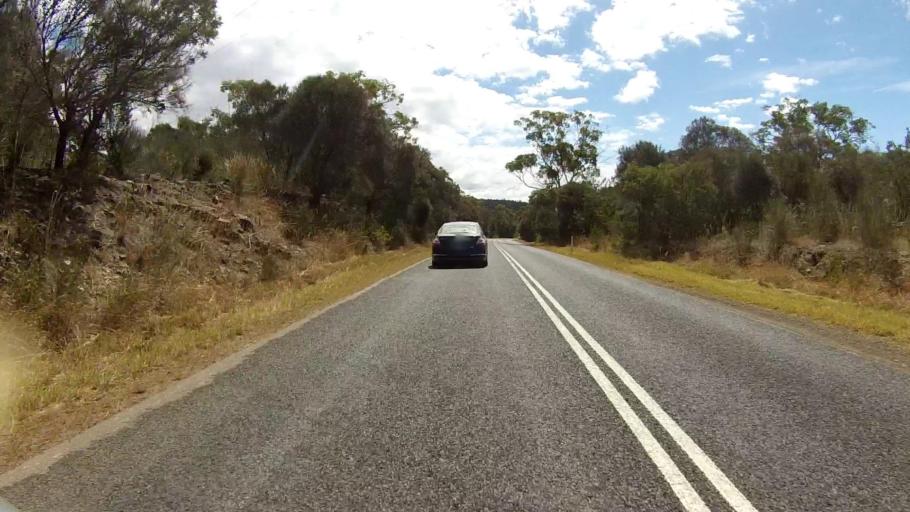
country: AU
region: Tasmania
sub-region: Sorell
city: Sorell
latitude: -42.1554
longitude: 148.0694
